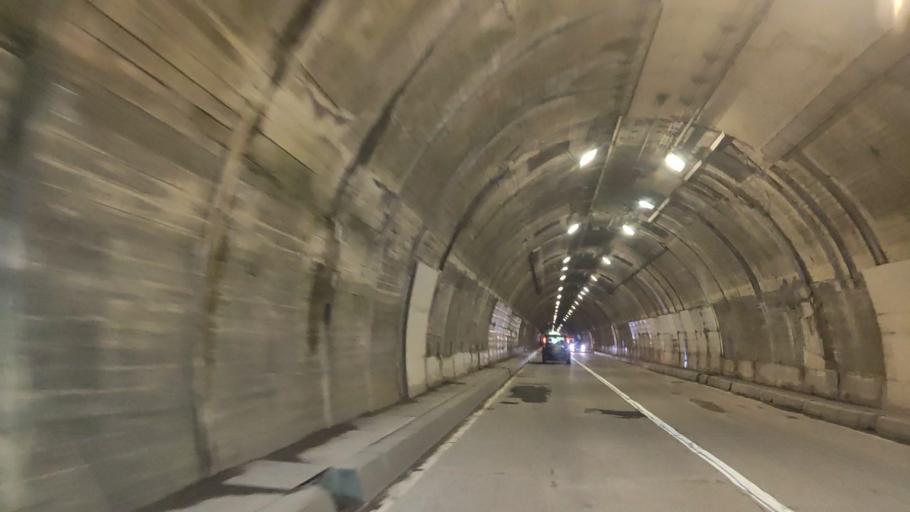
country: JP
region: Hokkaido
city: Niseko Town
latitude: 42.5902
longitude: 140.7012
